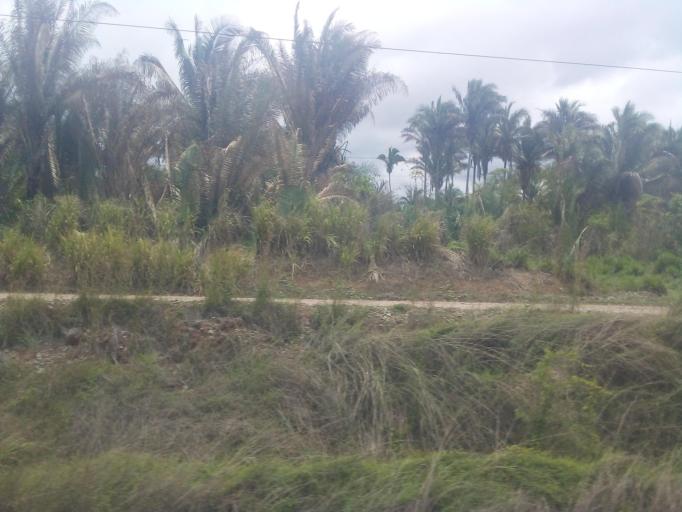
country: BR
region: Maranhao
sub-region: Pindare Mirim
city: Pindare Mirim
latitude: -3.6438
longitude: -45.2222
